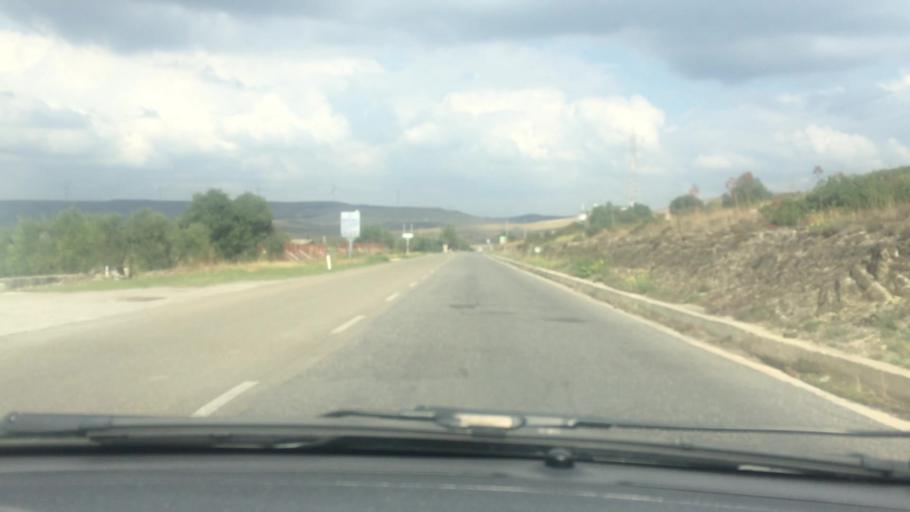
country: IT
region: Basilicate
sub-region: Provincia di Matera
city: Matera
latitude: 40.6839
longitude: 16.5708
